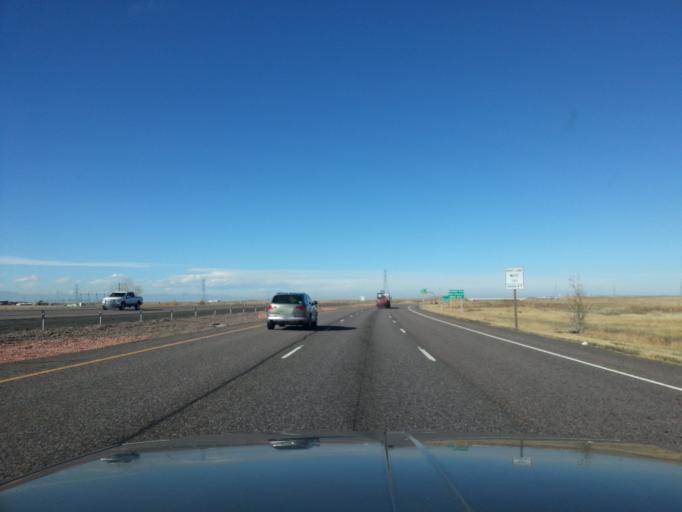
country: US
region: Colorado
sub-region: Adams County
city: Brighton
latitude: 39.8774
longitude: -104.7603
